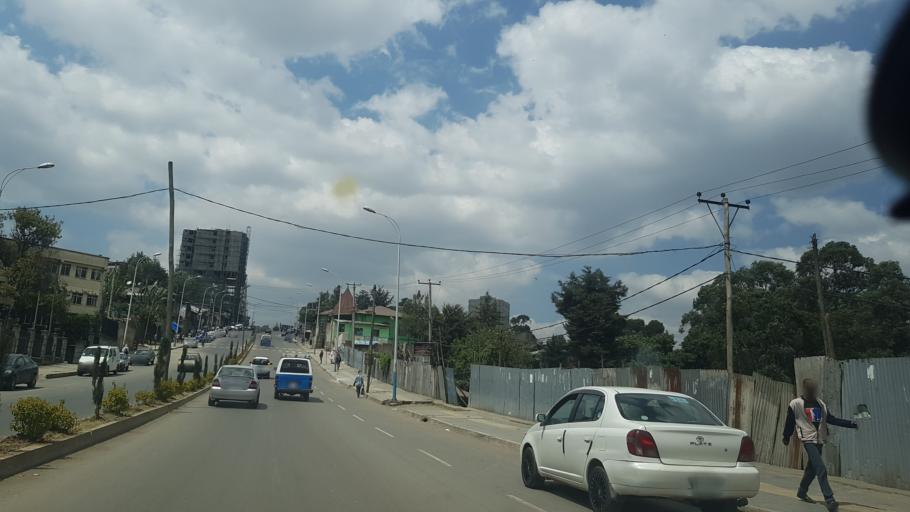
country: ET
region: Adis Abeba
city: Addis Ababa
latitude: 9.0280
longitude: 38.7491
